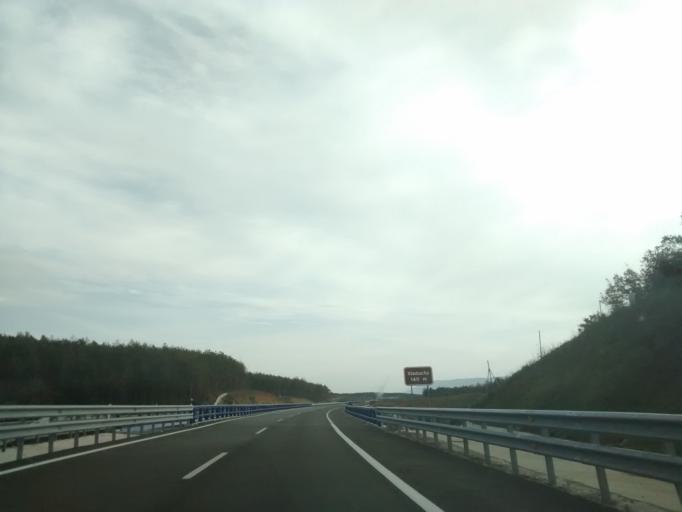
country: ES
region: Navarre
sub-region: Provincia de Navarra
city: Yesa
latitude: 42.6212
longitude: -1.1577
